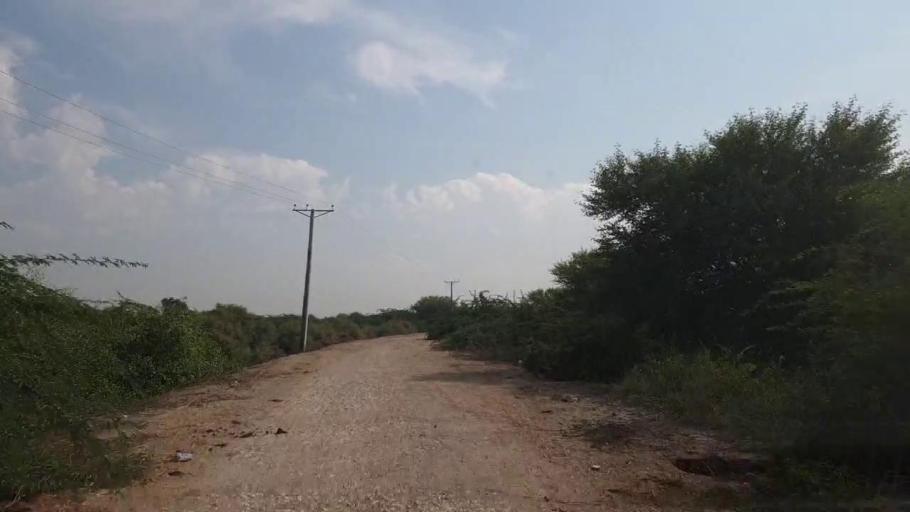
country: PK
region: Sindh
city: Tando Bago
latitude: 24.9324
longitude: 69.0057
